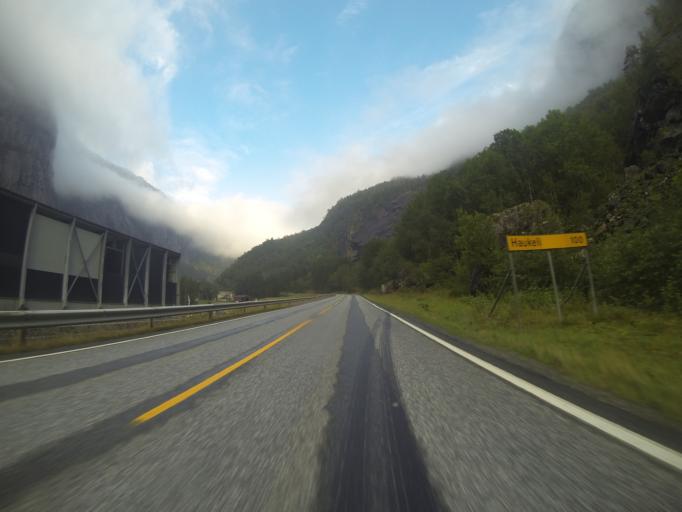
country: NO
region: Rogaland
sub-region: Sauda
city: Sauda
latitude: 59.8736
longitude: 6.3861
